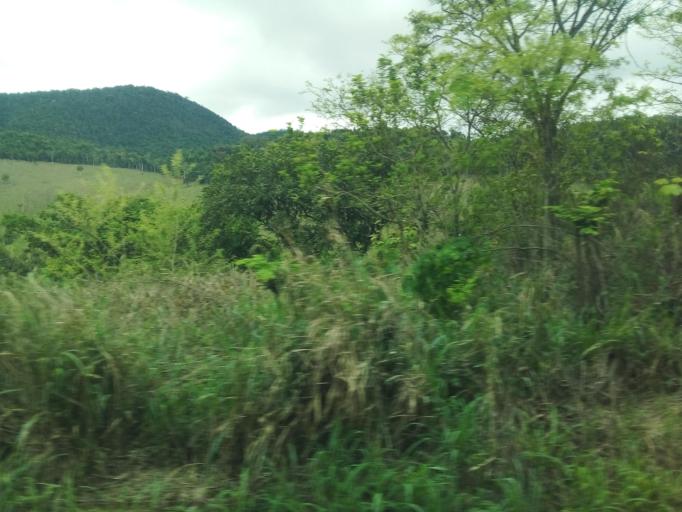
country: BR
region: Minas Gerais
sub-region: Nova Era
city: Nova Era
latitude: -19.6677
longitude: -42.8949
